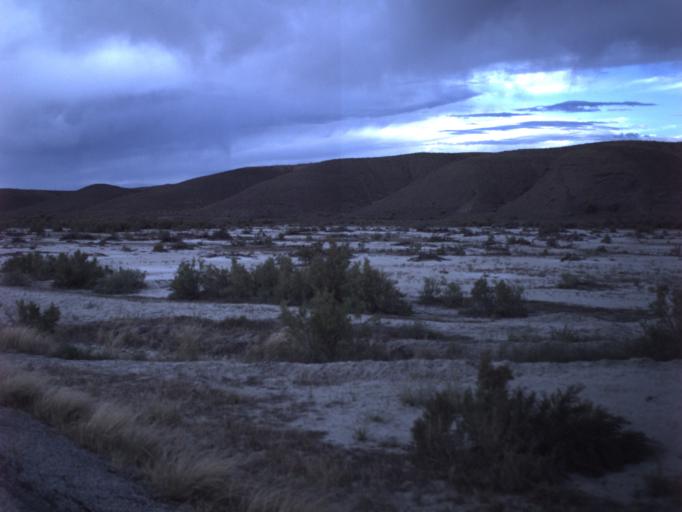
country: US
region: Utah
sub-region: Grand County
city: Moab
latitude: 38.8760
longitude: -109.3068
